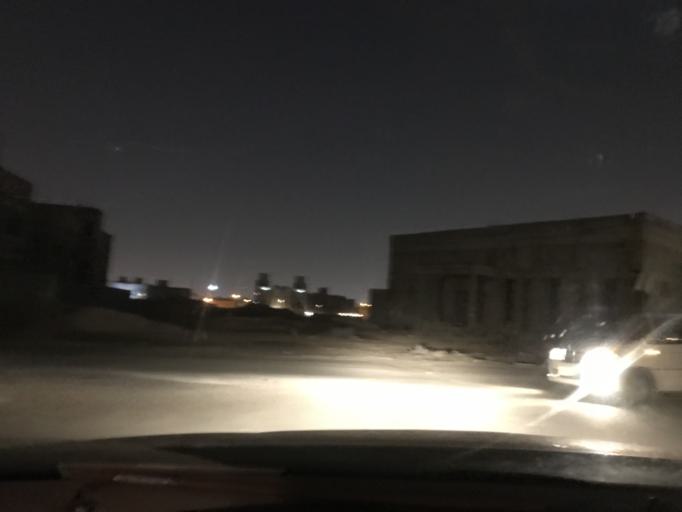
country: SA
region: Ar Riyad
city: Riyadh
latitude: 24.7495
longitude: 46.7555
